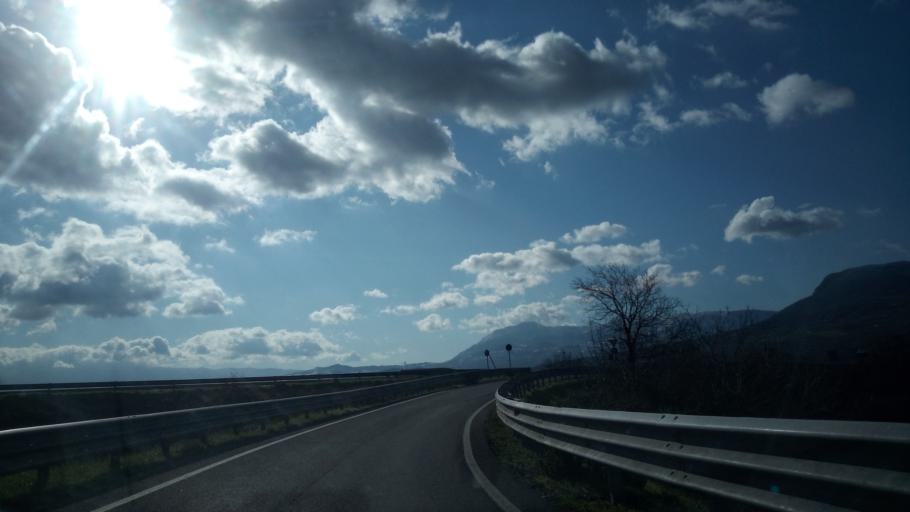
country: IT
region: Campania
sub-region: Provincia di Benevento
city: Ponte
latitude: 41.1885
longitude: 14.7406
